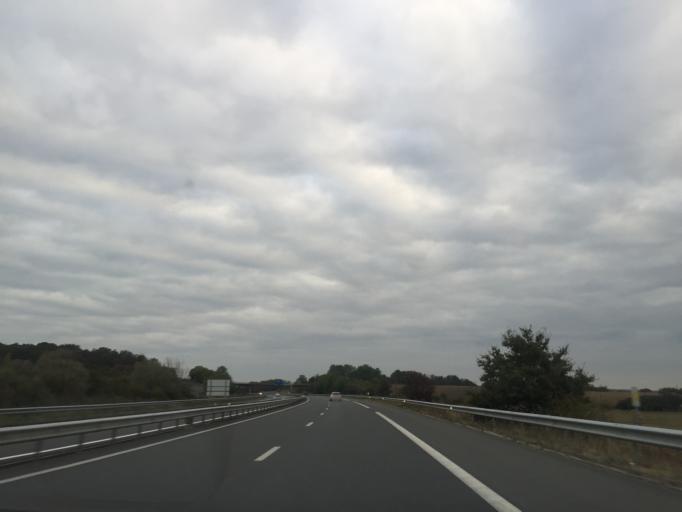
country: FR
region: Centre
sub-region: Departement du Cher
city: Orval
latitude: 46.7140
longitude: 2.4598
